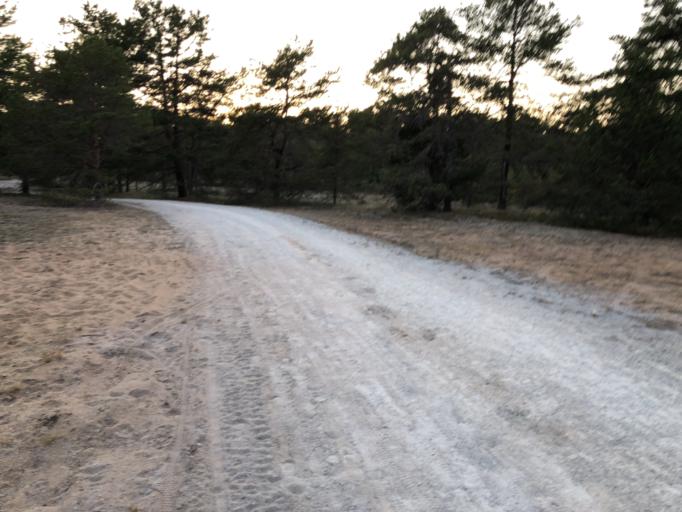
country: EE
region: Harju
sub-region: Paldiski linn
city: Paldiski
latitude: 59.3894
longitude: 24.2301
